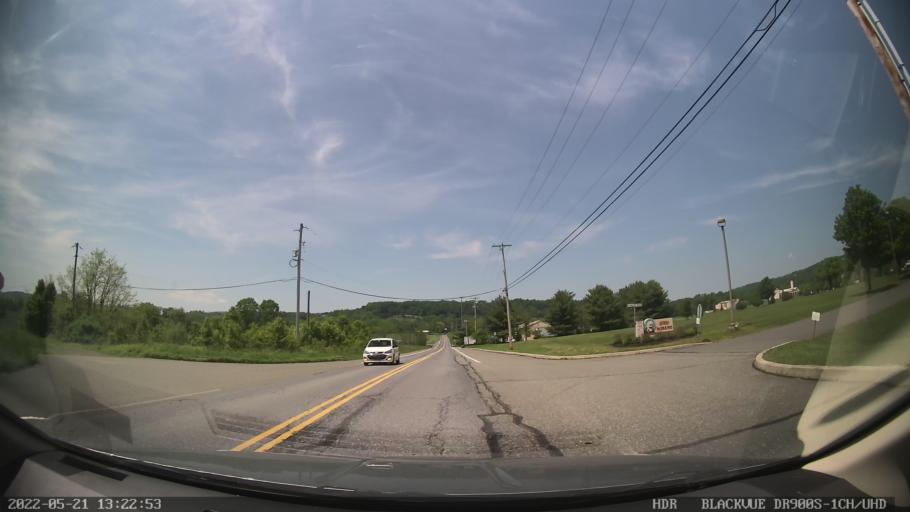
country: US
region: Pennsylvania
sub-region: Berks County
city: Bally
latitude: 40.3857
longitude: -75.6055
